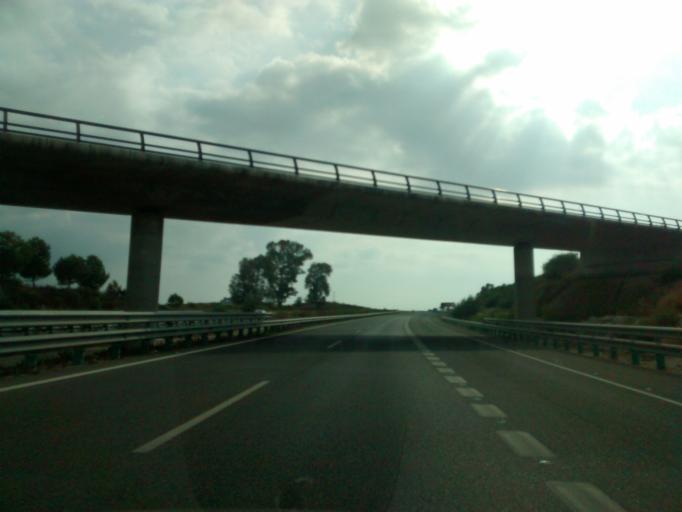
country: ES
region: Andalusia
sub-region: Provincia de Cadiz
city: Arcos de la Frontera
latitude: 36.7438
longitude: -5.8699
